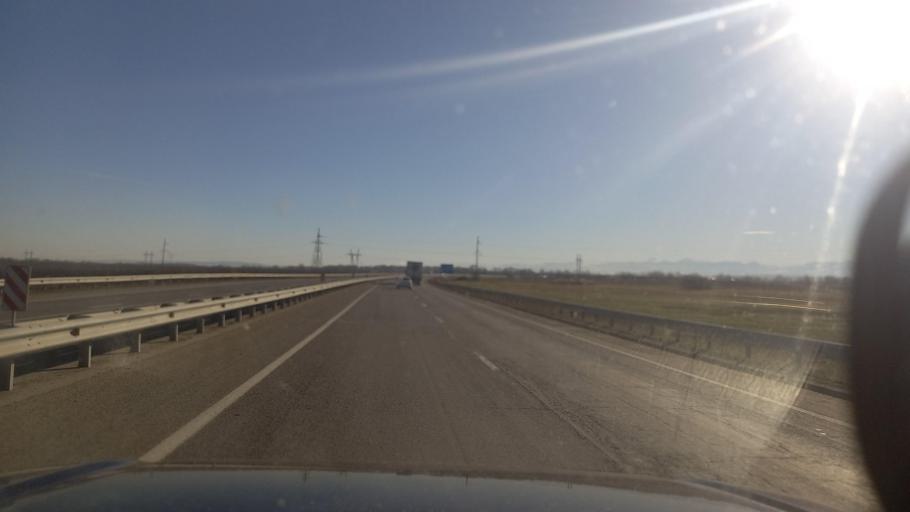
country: RU
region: Kabardino-Balkariya
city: Germenchik
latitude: 43.5735
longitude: 43.7099
